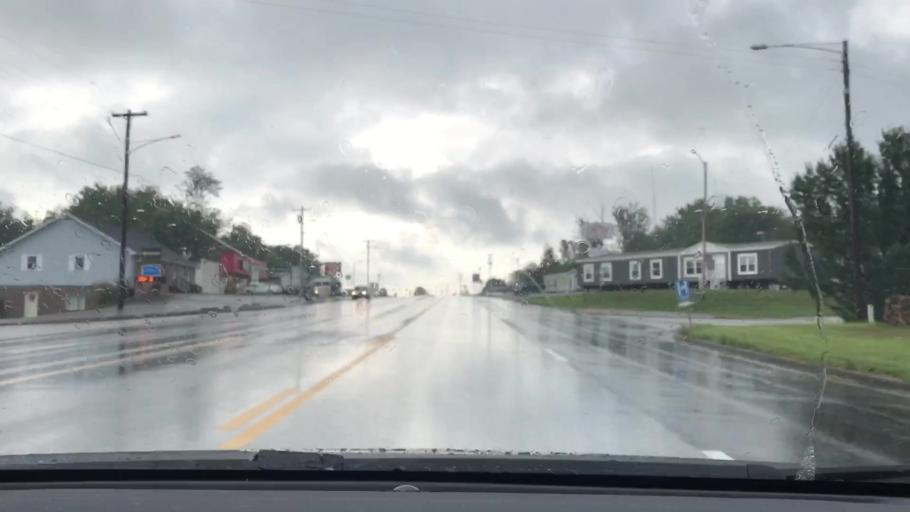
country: US
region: Tennessee
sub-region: Macon County
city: Lafayette
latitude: 36.5175
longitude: -86.0278
